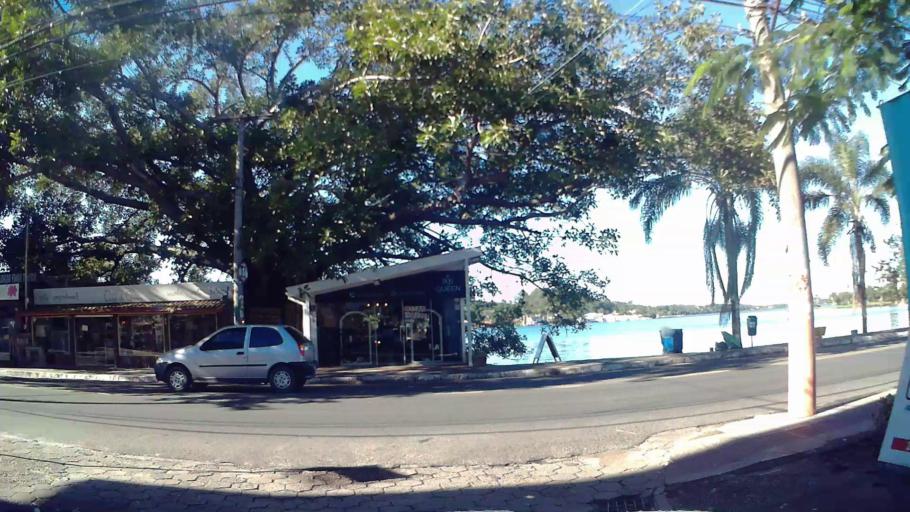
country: BR
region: Santa Catarina
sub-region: Florianopolis
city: Lagoa
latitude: -27.6046
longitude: -48.4655
